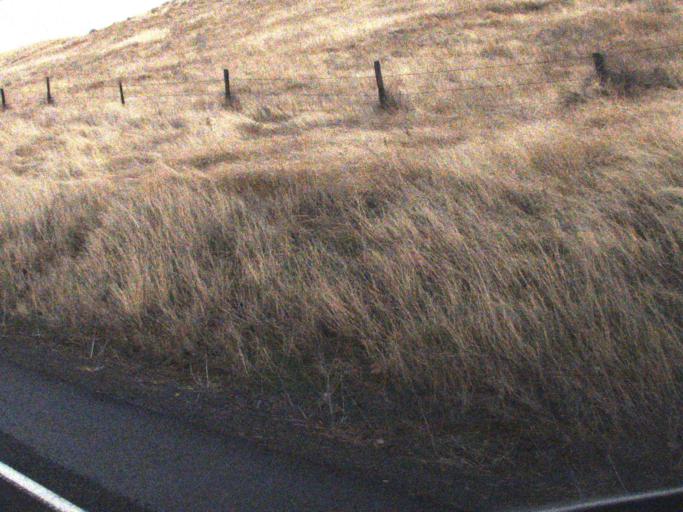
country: US
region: Washington
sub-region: Columbia County
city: Dayton
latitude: 46.5097
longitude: -117.9615
